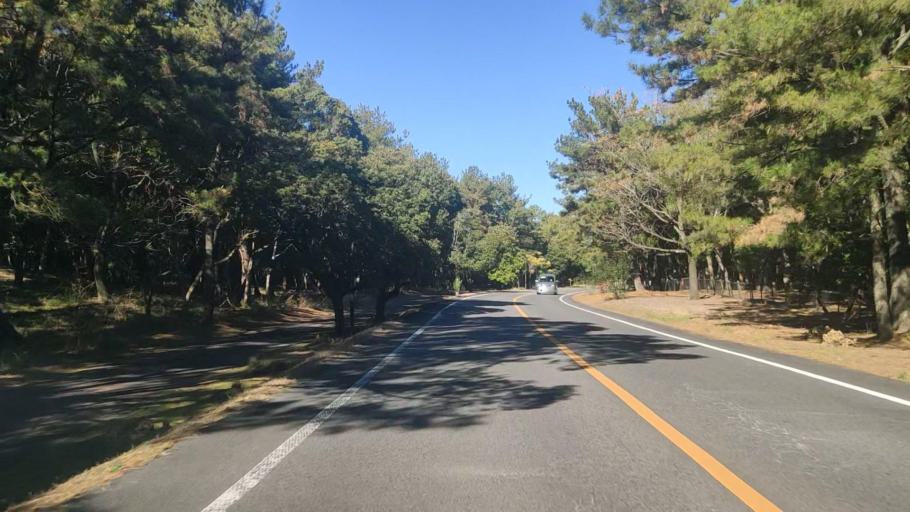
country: JP
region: Miyazaki
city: Miyazaki-shi
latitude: 31.9456
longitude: 131.4648
